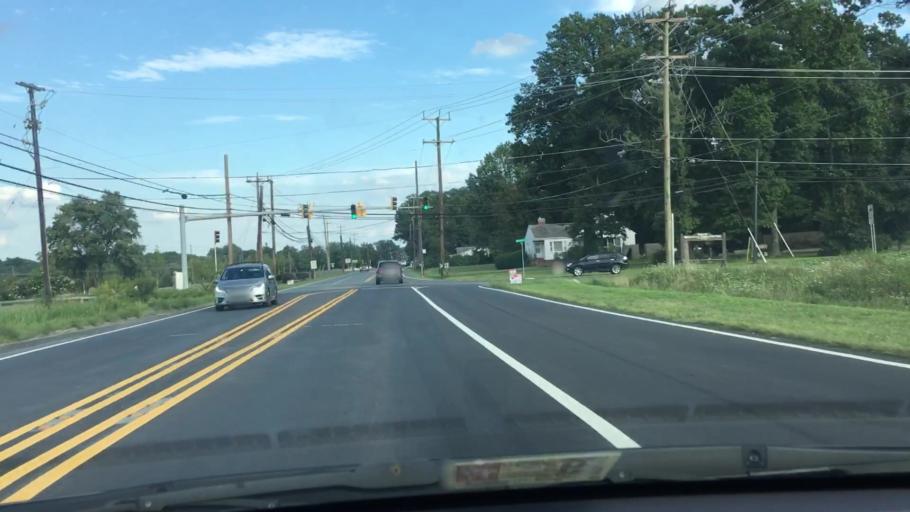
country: US
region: Maryland
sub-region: Montgomery County
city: Redland
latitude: 39.1841
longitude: -77.1128
